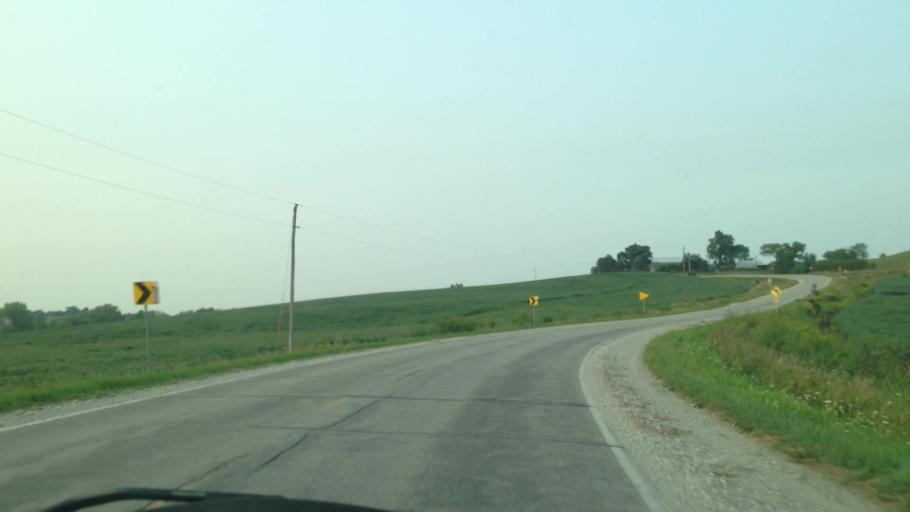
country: US
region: Iowa
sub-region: Iowa County
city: Marengo
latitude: 41.8618
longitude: -92.0914
